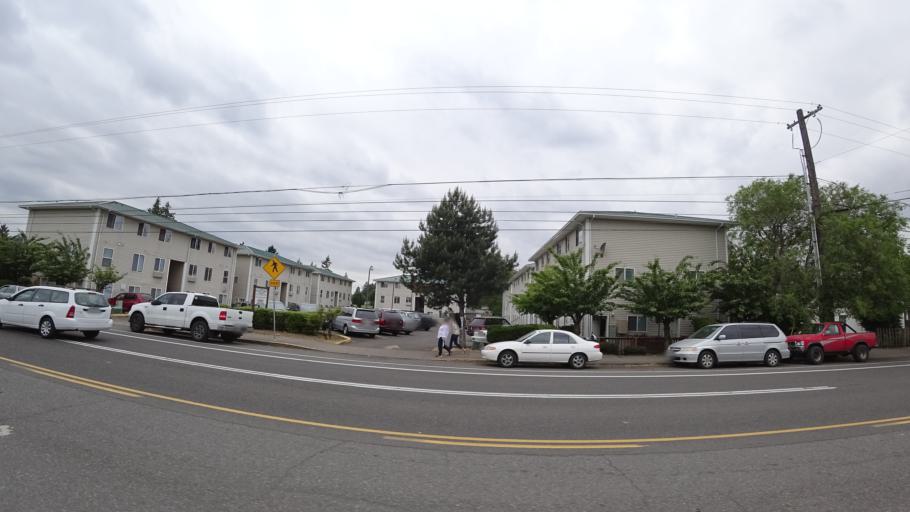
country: US
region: Oregon
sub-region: Multnomah County
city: Lents
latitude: 45.5098
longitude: -122.5377
